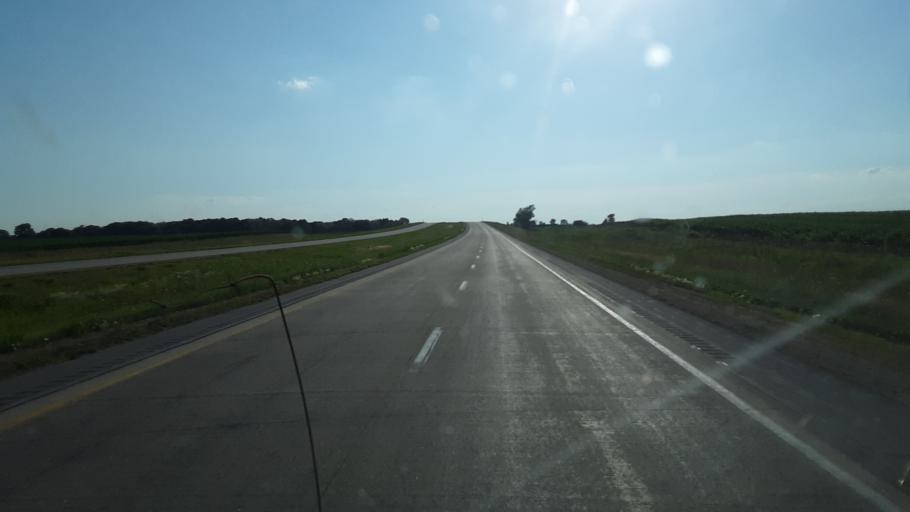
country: US
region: Iowa
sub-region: Hardin County
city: Iowa Falls
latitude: 42.4487
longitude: -93.3474
